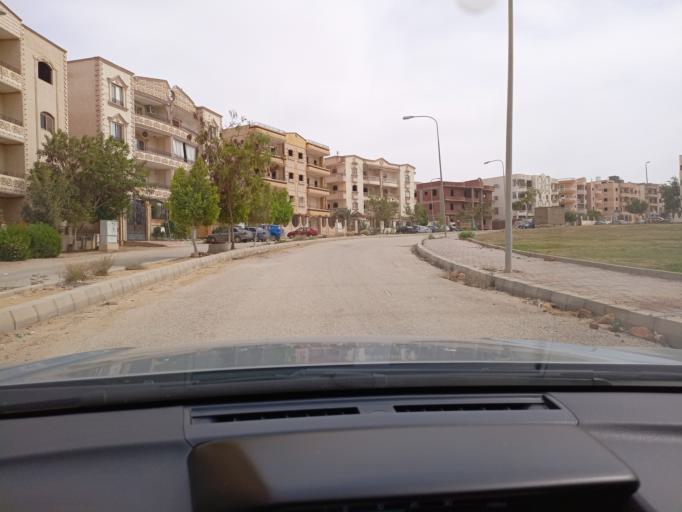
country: EG
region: Muhafazat al Qalyubiyah
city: Al Khankah
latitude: 30.2438
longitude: 31.4885
